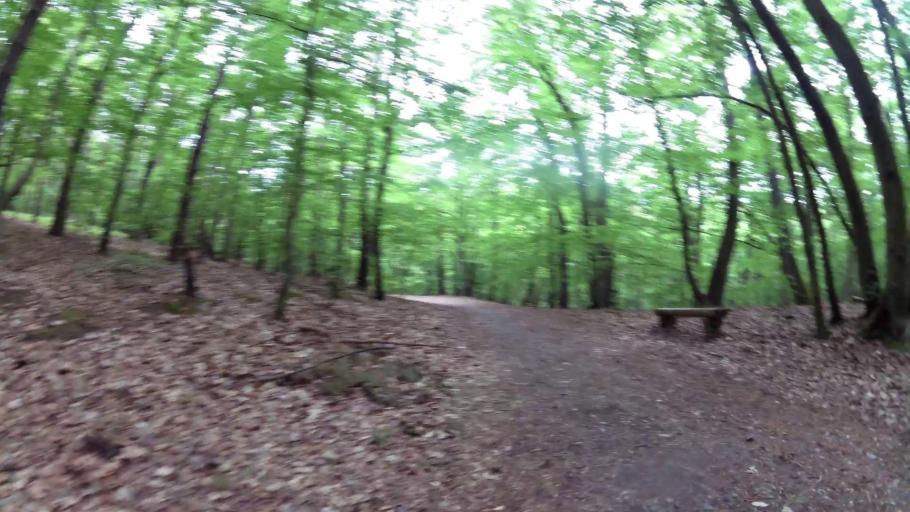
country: PL
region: West Pomeranian Voivodeship
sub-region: Powiat kamienski
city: Miedzyzdroje
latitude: 53.9336
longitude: 14.4607
